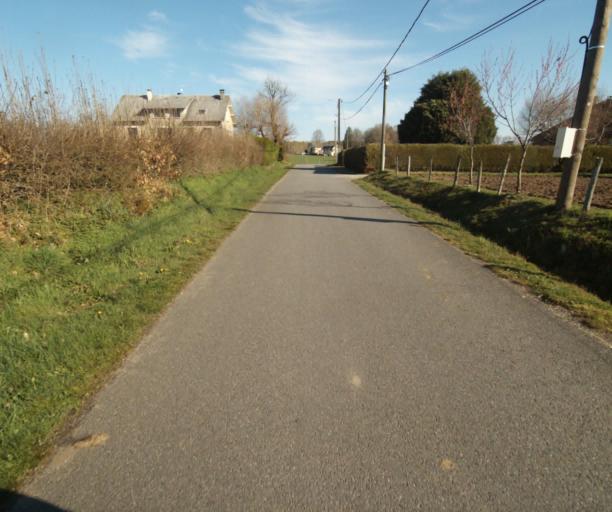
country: FR
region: Limousin
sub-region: Departement de la Correze
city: Correze
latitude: 45.3180
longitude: 1.8886
